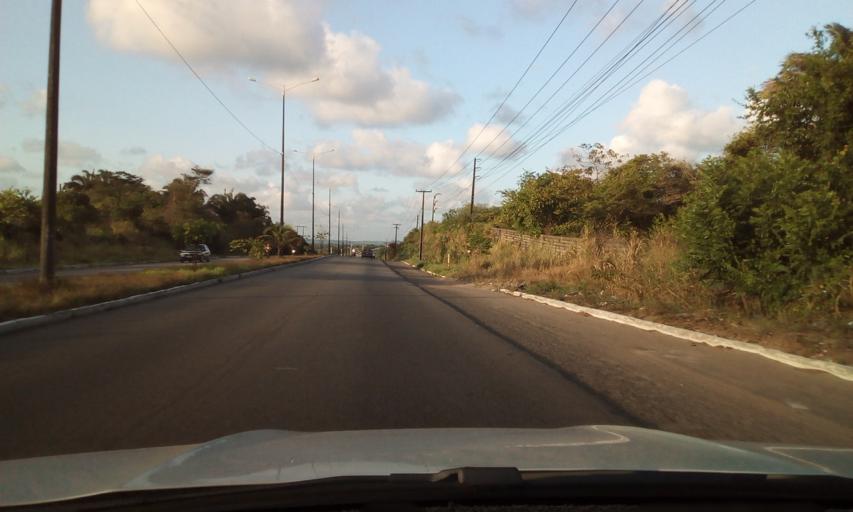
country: BR
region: Paraiba
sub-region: Bayeux
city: Bayeux
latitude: -7.1423
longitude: -34.9057
